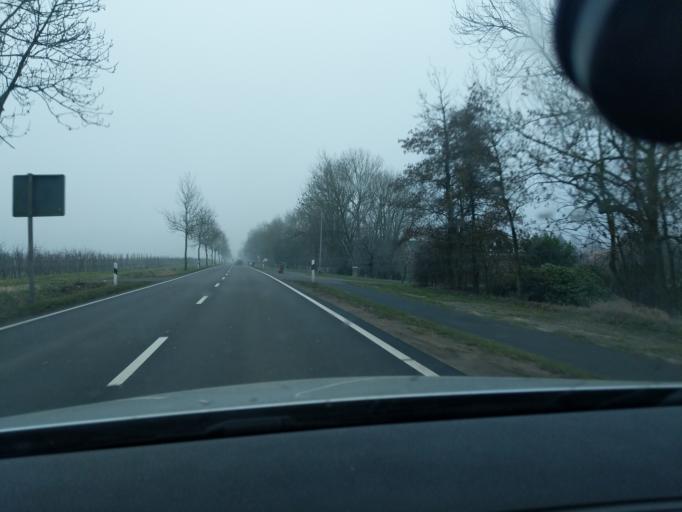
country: DE
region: Lower Saxony
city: Jork
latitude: 53.5481
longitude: 9.6689
